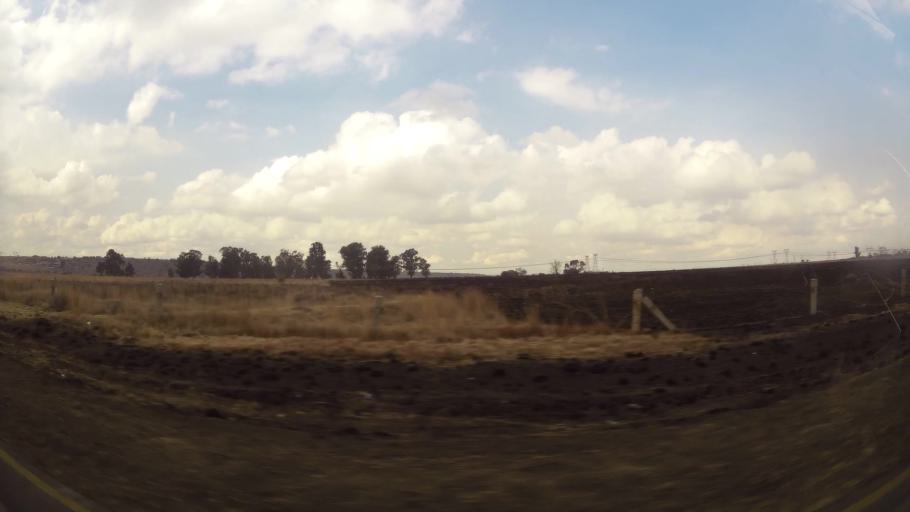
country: ZA
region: Orange Free State
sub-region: Fezile Dabi District Municipality
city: Sasolburg
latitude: -26.8125
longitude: 27.9094
